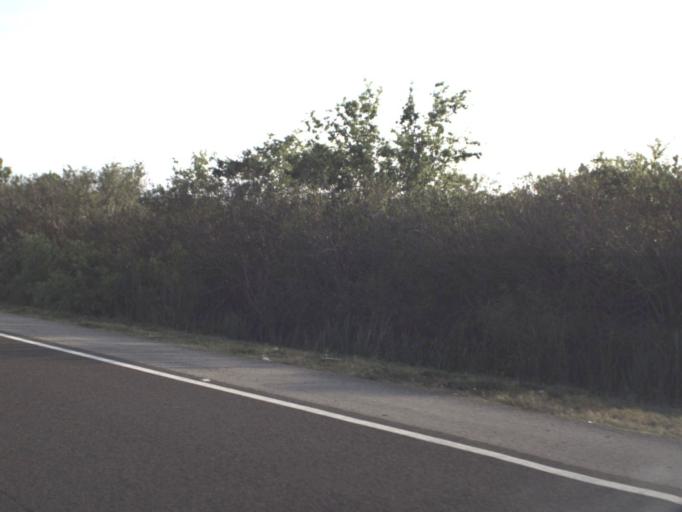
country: US
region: Florida
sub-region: Brevard County
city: Titusville
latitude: 28.5466
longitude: -80.8518
